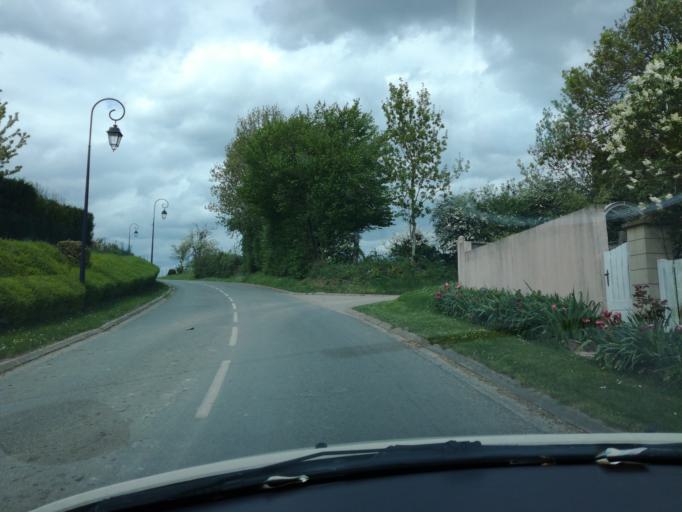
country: FR
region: Picardie
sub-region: Departement de la Somme
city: Poix-de-Picardie
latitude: 49.8211
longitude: 2.0204
